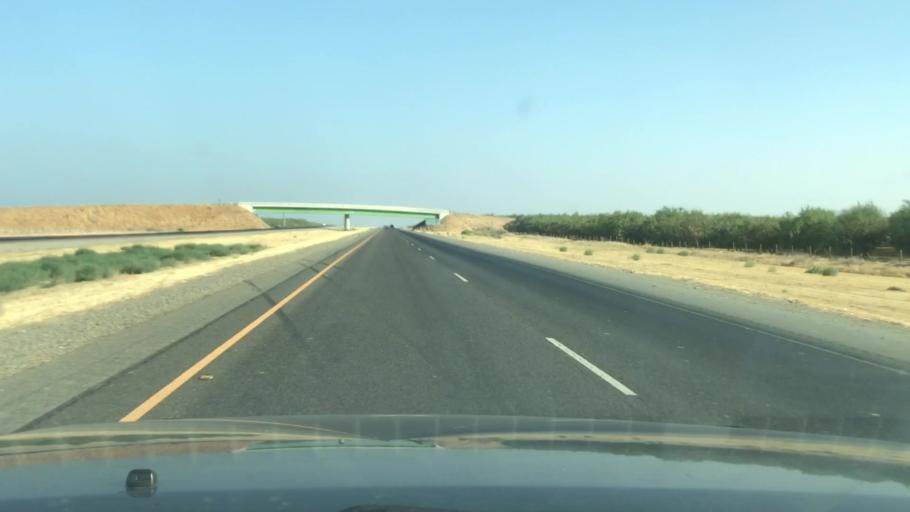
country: US
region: California
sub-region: Merced County
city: South Dos Palos
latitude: 36.7632
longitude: -120.7141
